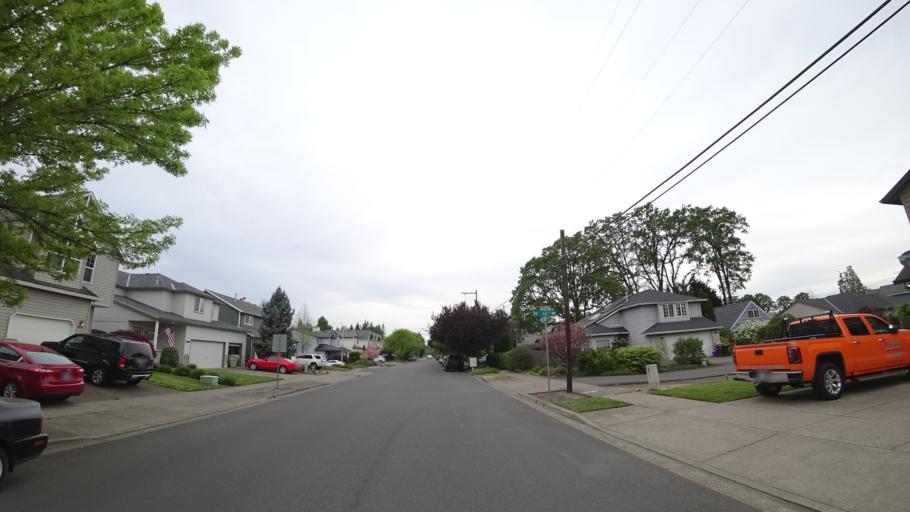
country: US
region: Oregon
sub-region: Washington County
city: Aloha
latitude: 45.5123
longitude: -122.9116
